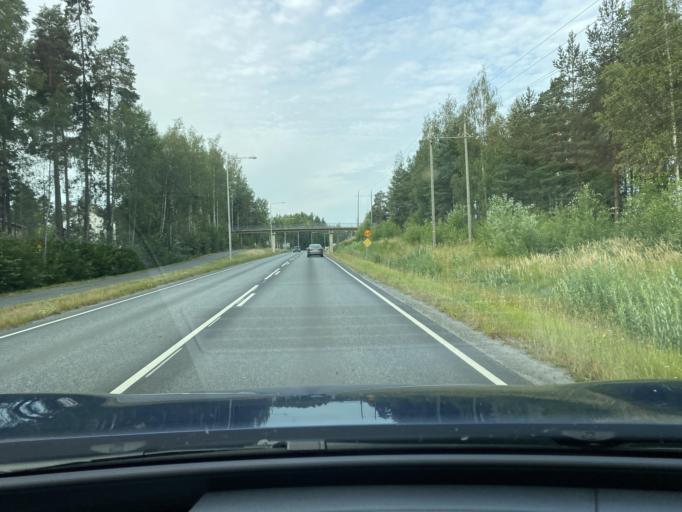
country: FI
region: Pirkanmaa
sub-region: Lounais-Pirkanmaa
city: Vammala
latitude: 61.3549
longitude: 22.8904
